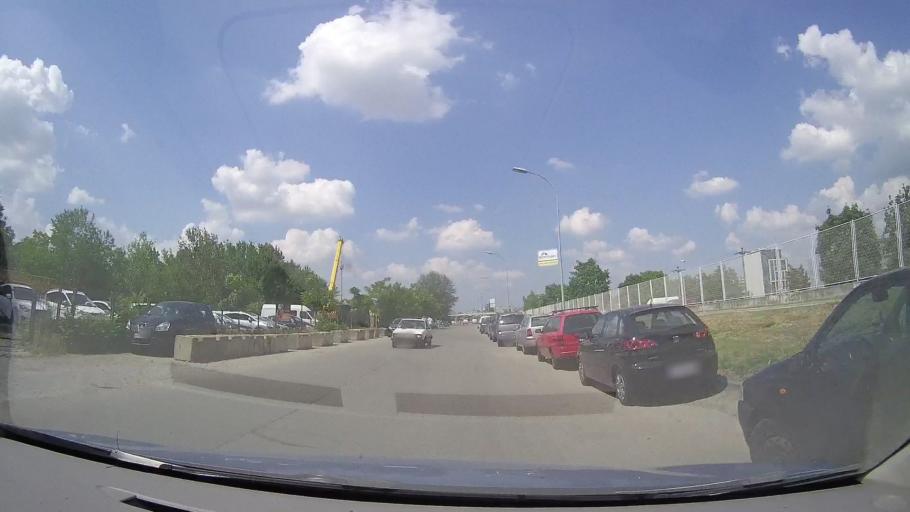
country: RS
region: Central Serbia
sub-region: Belgrade
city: Novi Beograd
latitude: 44.8018
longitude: 20.4175
